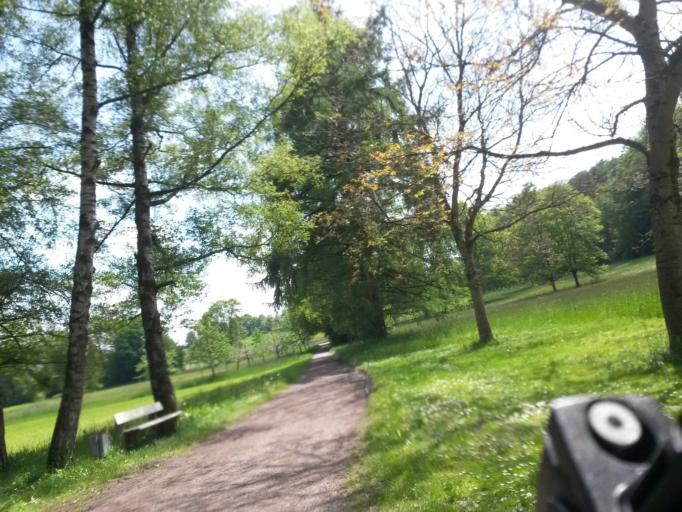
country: DE
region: Baden-Wuerttemberg
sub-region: Tuebingen Region
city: Bad Waldsee
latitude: 47.9119
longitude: 9.7594
